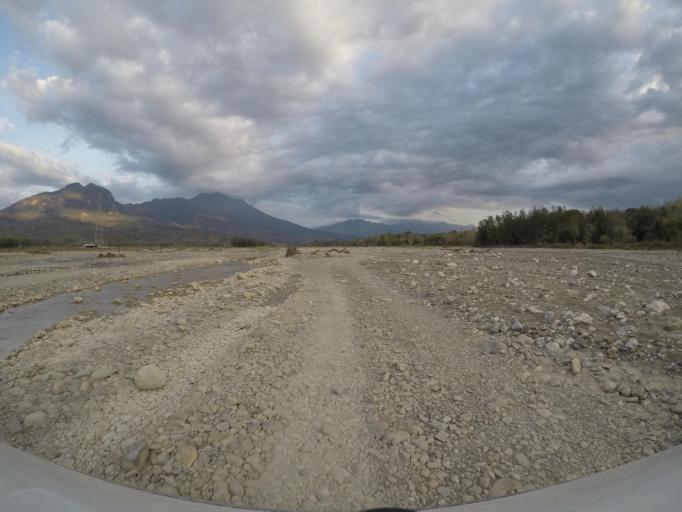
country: TL
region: Bobonaro
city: Maliana
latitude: -8.9044
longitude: 125.2099
